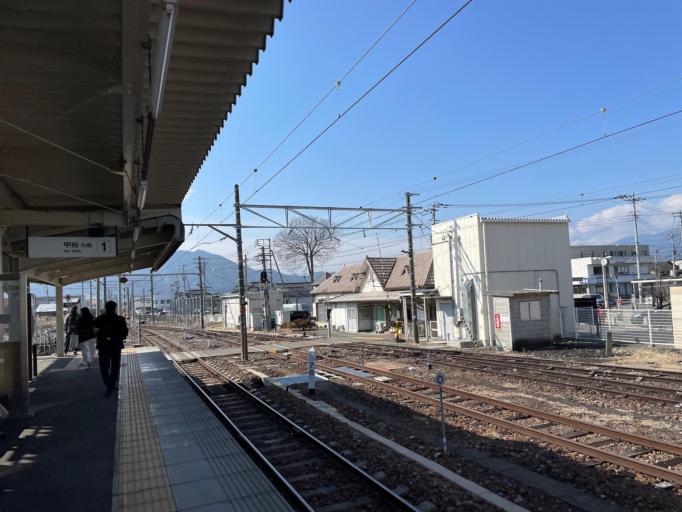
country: JP
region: Yamanashi
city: Ryuo
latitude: 35.5947
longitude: 138.5269
